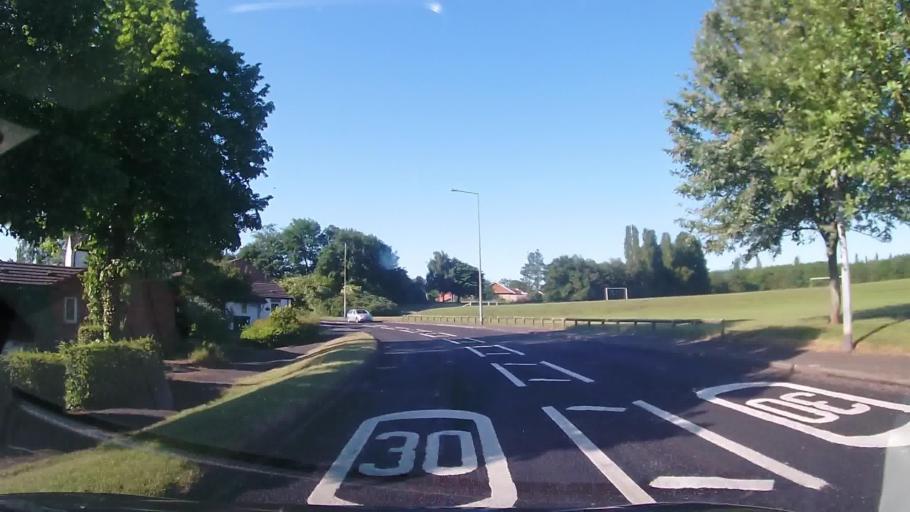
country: GB
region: England
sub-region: Telford and Wrekin
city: Wellington
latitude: 52.7084
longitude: -2.5013
